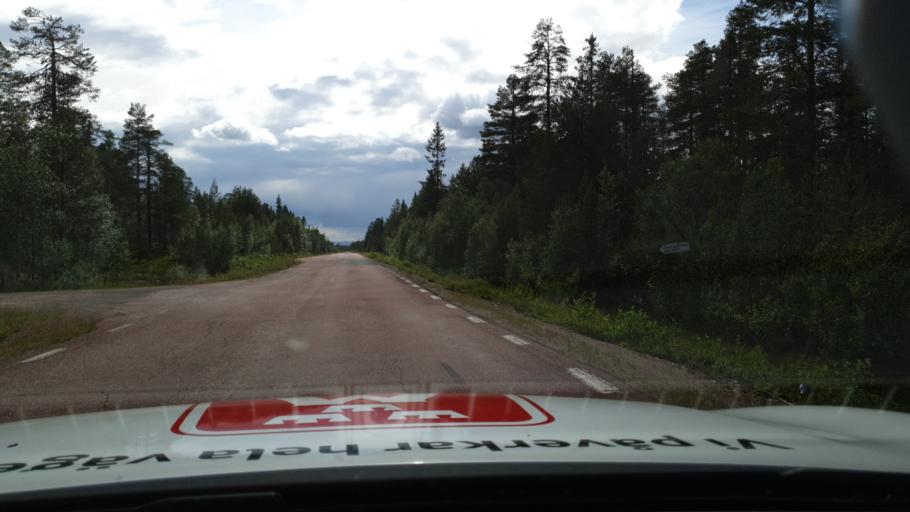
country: SE
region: Dalarna
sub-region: Alvdalens Kommun
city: AElvdalen
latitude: 61.7646
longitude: 13.4712
